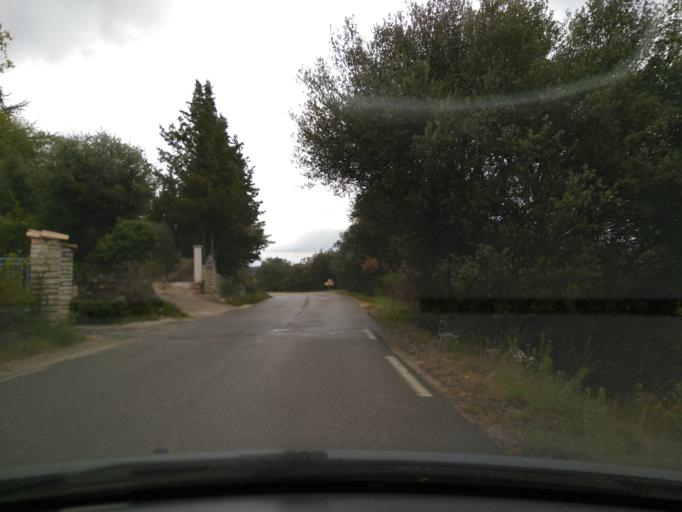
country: FR
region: Languedoc-Roussillon
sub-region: Departement du Gard
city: Barjac
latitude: 44.3503
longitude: 4.4053
